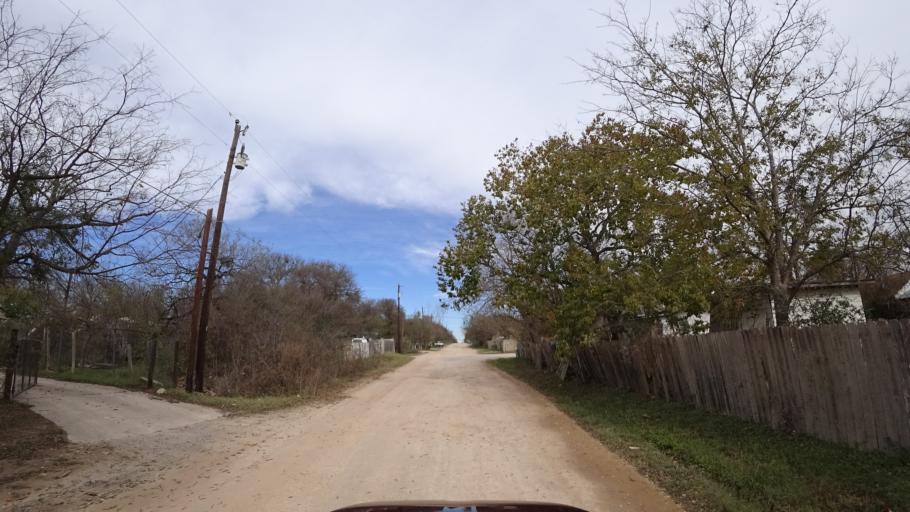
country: US
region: Texas
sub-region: Travis County
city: Garfield
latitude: 30.1326
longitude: -97.5718
